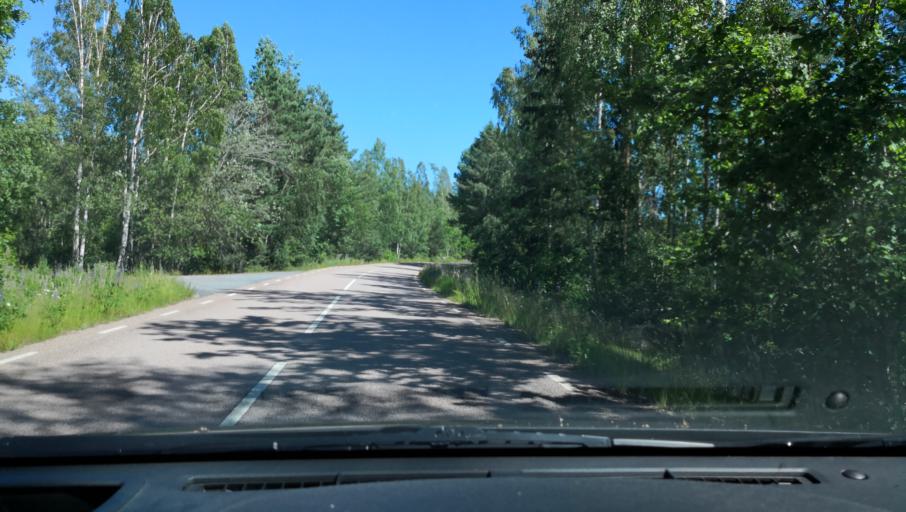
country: SE
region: Vaestmanland
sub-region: Arboga Kommun
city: Tyringe
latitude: 59.3046
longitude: 16.0072
